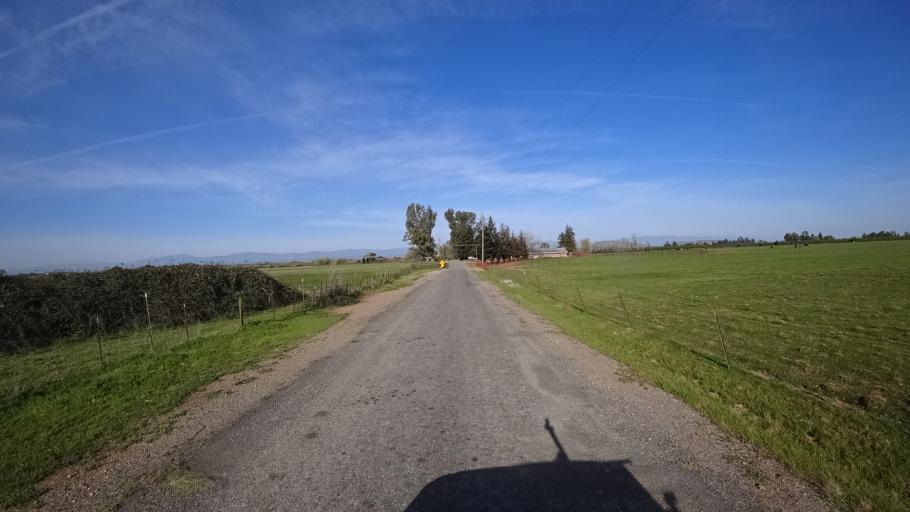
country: US
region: California
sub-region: Glenn County
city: Orland
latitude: 39.7189
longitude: -122.2433
